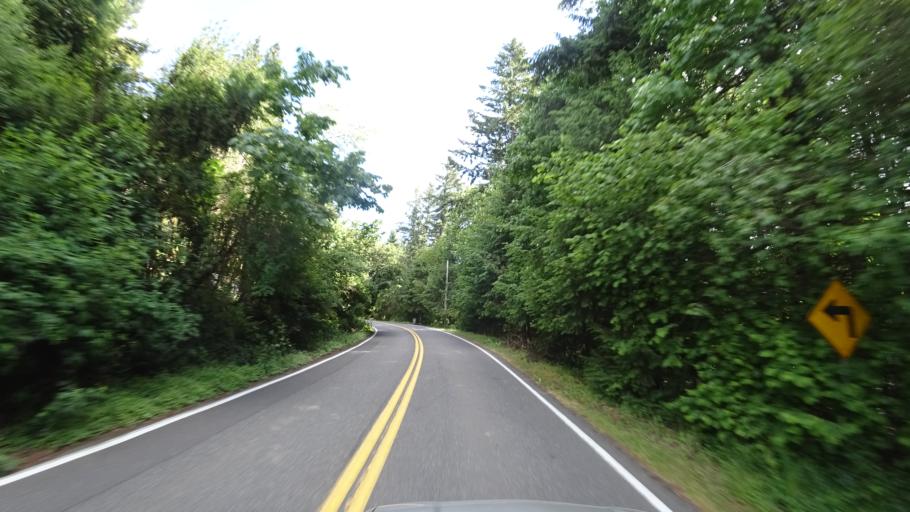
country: US
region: Oregon
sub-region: Washington County
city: Oak Hills
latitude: 45.5952
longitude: -122.8193
